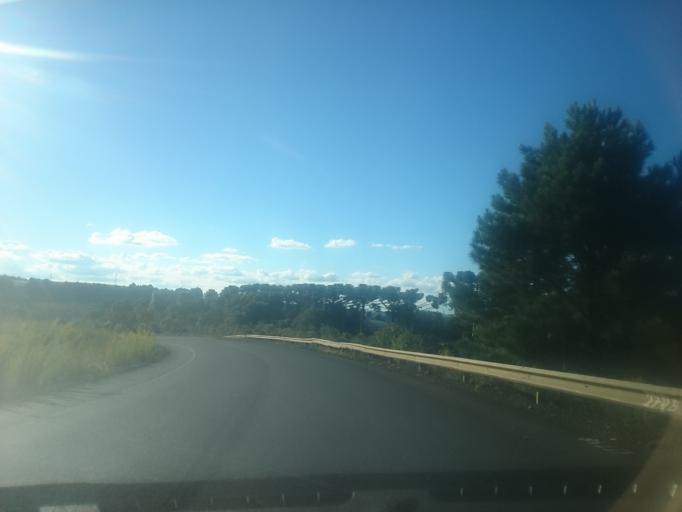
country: BR
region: Santa Catarina
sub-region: Sao Joaquim
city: Sao Joaquim
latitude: -28.1911
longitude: -49.9957
